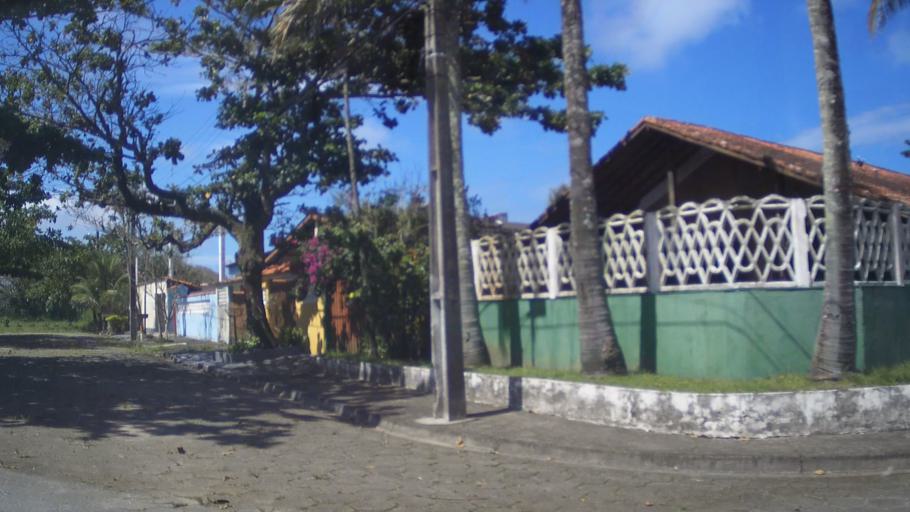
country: BR
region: Sao Paulo
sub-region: Itanhaem
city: Itanhaem
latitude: -24.1463
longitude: -46.7179
